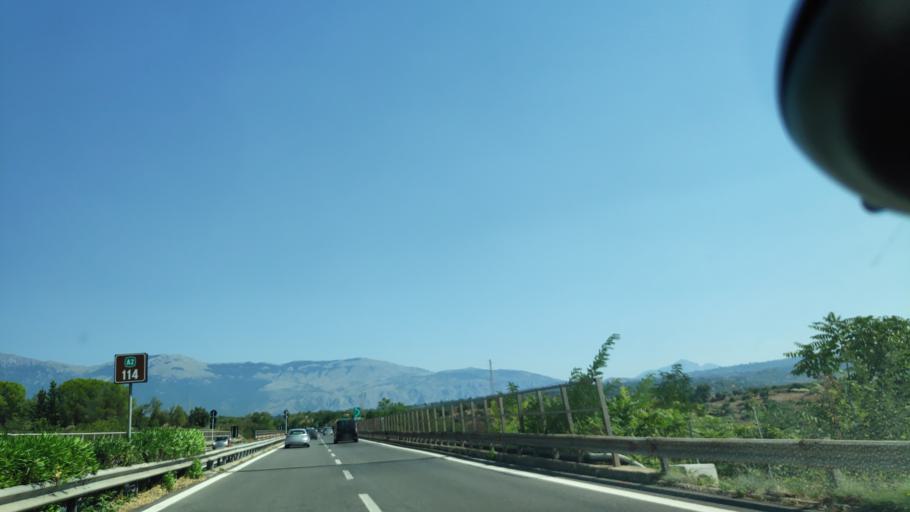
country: IT
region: Calabria
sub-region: Provincia di Cosenza
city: Castrovillari
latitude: 39.7662
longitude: 16.2213
